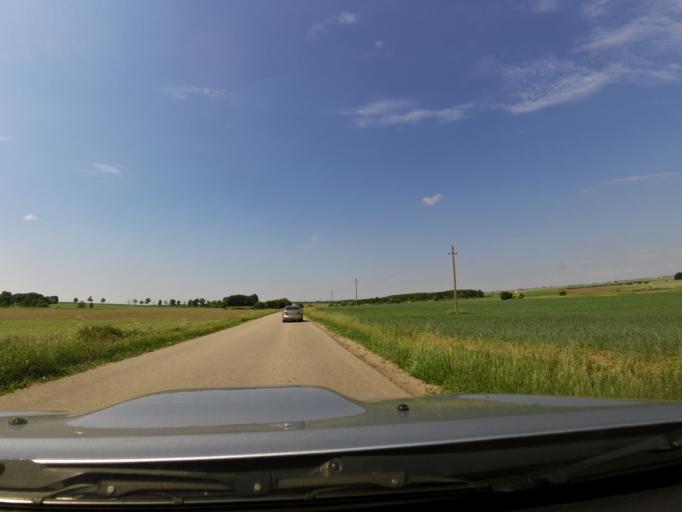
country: LT
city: Vilkaviskis
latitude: 54.5053
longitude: 23.0057
